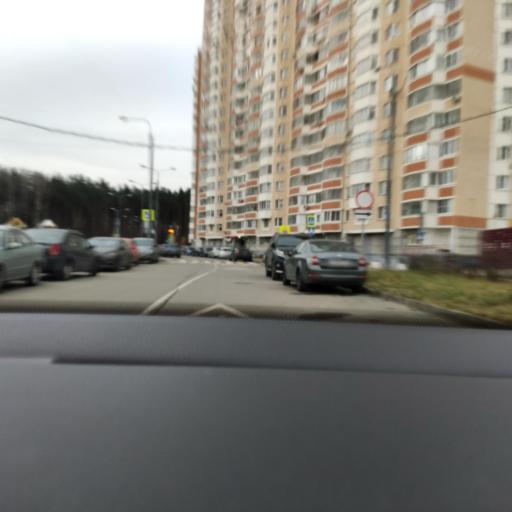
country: RU
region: Moscow
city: Vostochnyy
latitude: 55.8226
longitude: 37.8912
